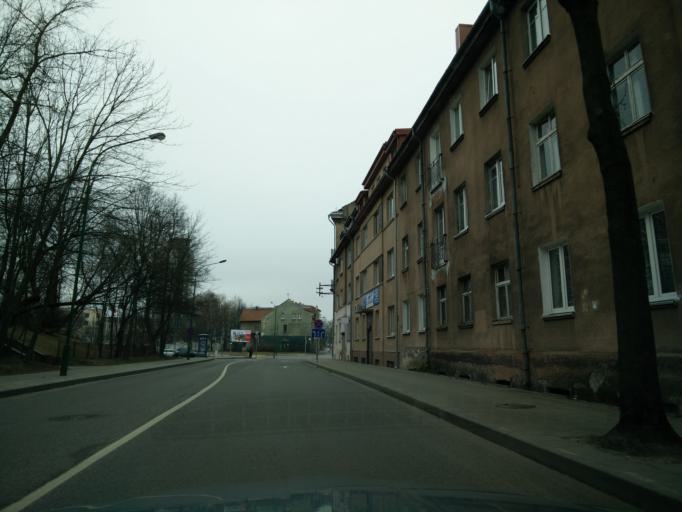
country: LT
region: Klaipedos apskritis
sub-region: Klaipeda
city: Klaipeda
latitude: 55.7034
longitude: 21.1375
